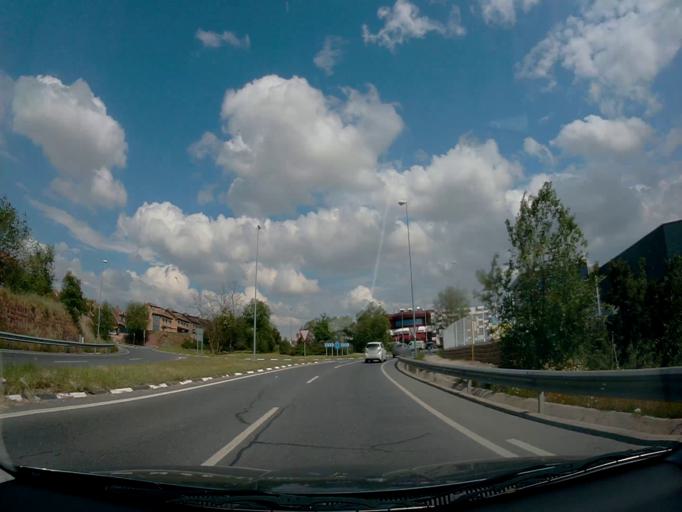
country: ES
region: Madrid
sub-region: Provincia de Madrid
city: Villaviciosa de Odon
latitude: 40.3519
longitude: -3.8823
